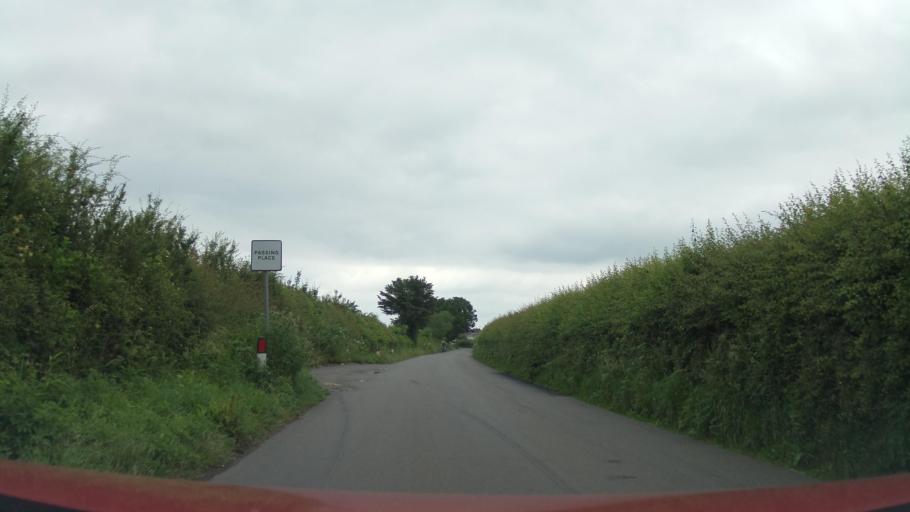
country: GB
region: England
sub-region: Derbyshire
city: Rodsley
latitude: 52.8732
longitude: -1.7146
